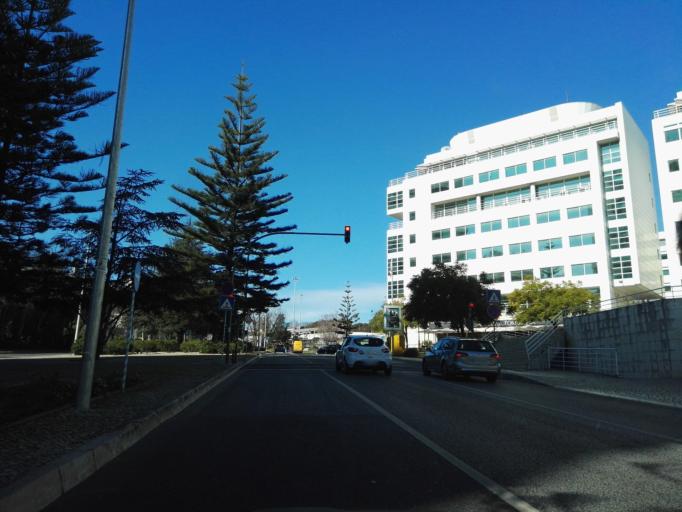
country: PT
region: Lisbon
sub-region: Oeiras
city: Alges
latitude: 38.7145
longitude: -9.2275
